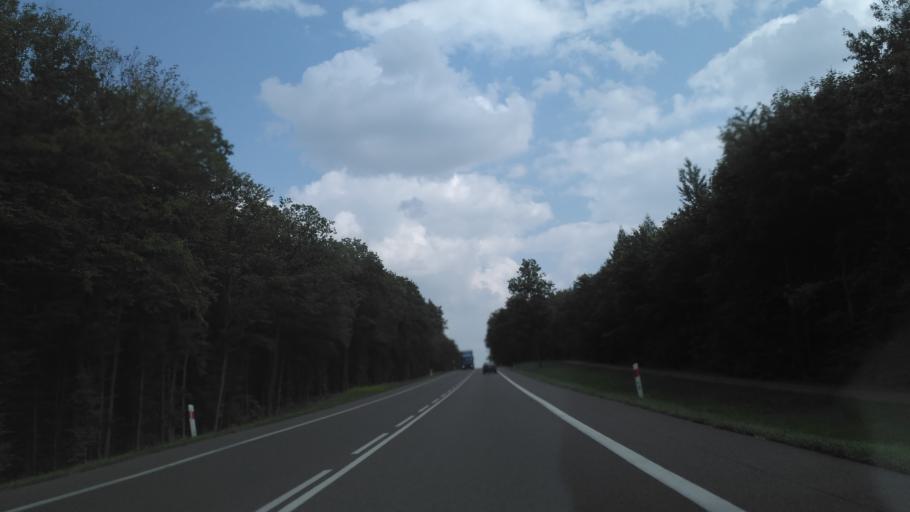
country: PL
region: Lublin Voivodeship
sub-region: Chelm
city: Chelm
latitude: 51.1555
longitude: 23.4095
